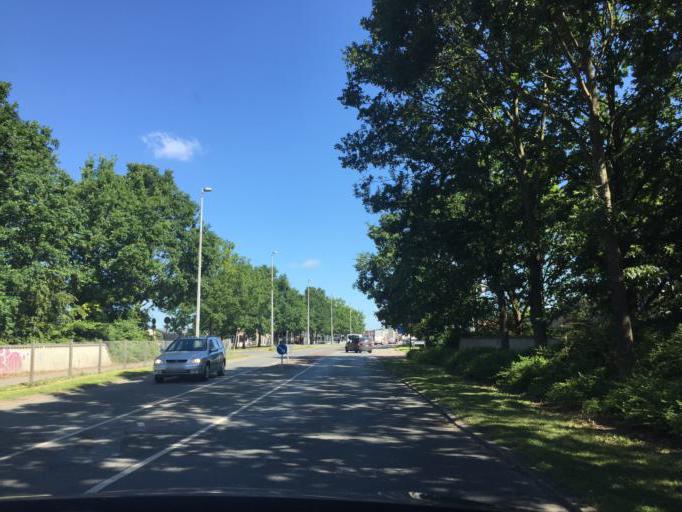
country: DK
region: South Denmark
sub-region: Odense Kommune
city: Odense
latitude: 55.3920
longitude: 10.3650
